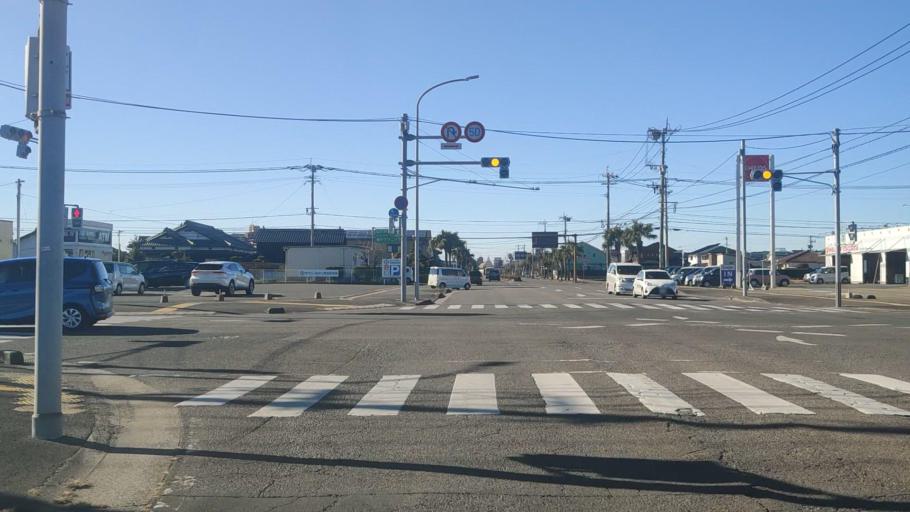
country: JP
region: Miyazaki
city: Miyazaki-shi
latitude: 31.9423
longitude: 131.4410
